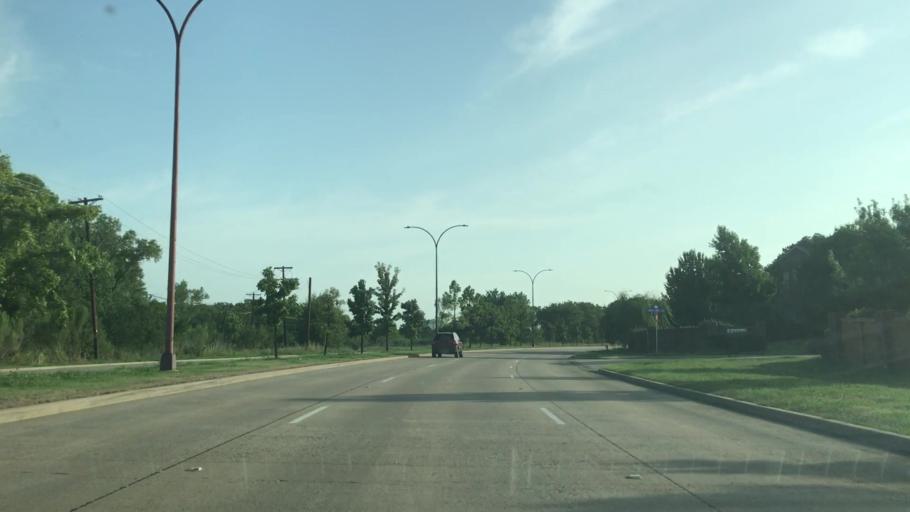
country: US
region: Texas
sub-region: Tarrant County
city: Arlington
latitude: 32.7689
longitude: -97.1479
